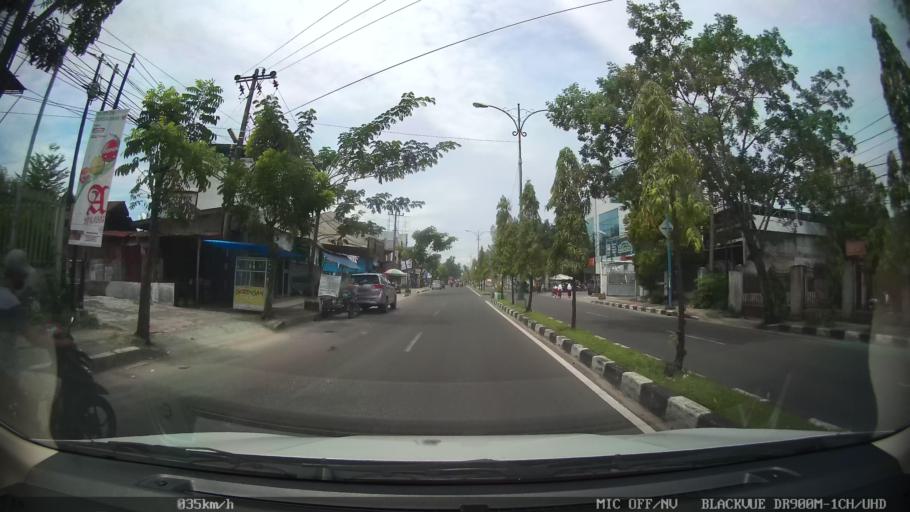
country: ID
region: North Sumatra
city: Sunggal
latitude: 3.5511
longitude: 98.6298
